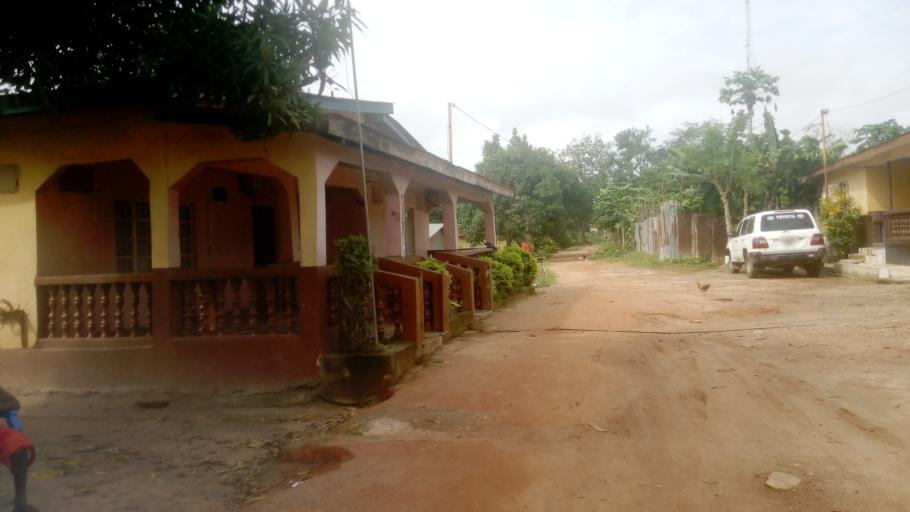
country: SL
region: Northern Province
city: Lunsar
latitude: 8.6932
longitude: -12.5349
